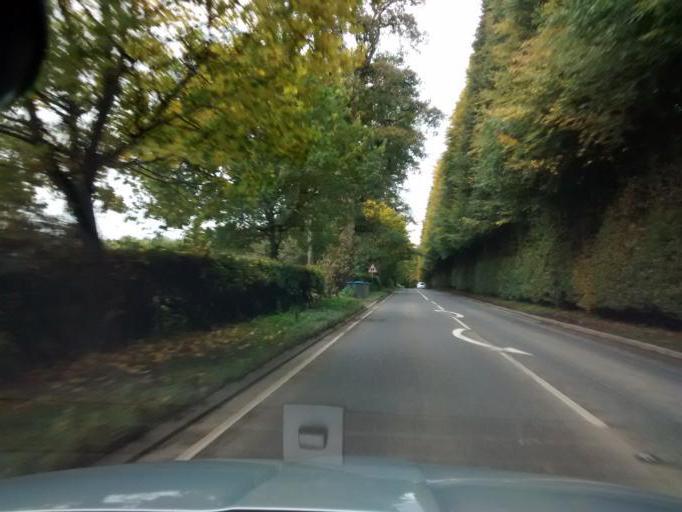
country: GB
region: Scotland
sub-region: Perth and Kinross
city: Blairgowrie
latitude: 56.5335
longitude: -3.3640
